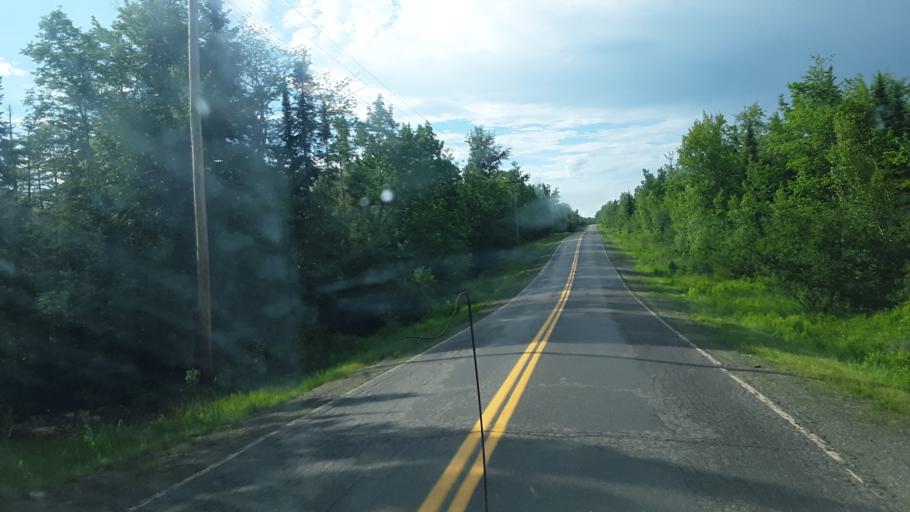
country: US
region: Maine
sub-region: Washington County
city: Calais
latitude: 45.1947
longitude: -67.5239
